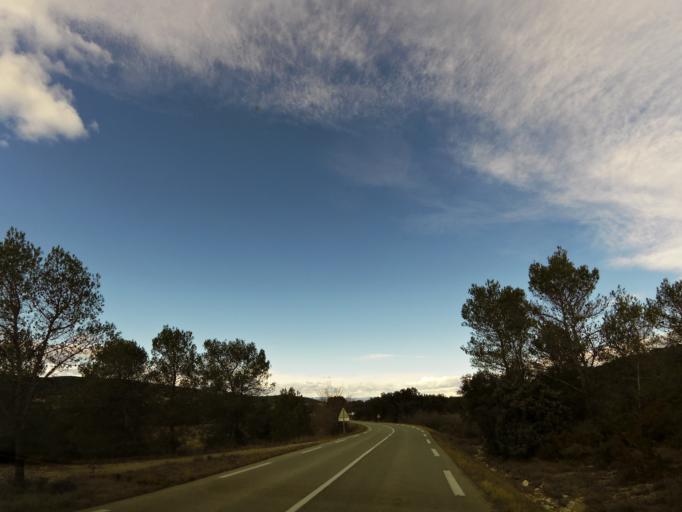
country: FR
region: Languedoc-Roussillon
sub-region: Departement du Gard
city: Quissac
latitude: 43.8444
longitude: 4.0212
